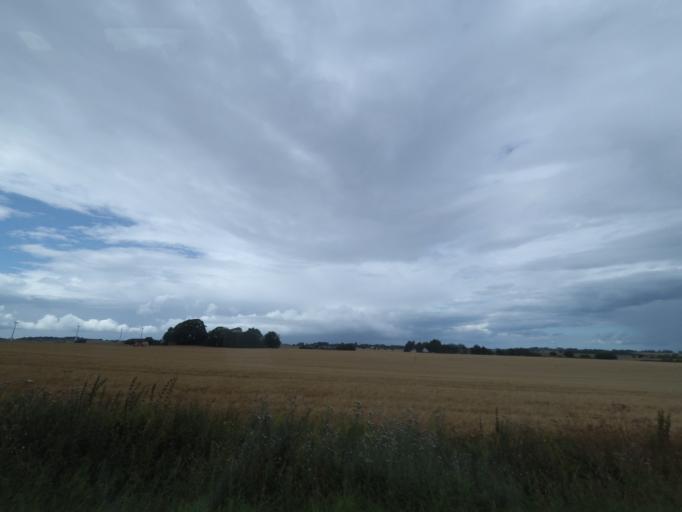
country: DK
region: South Denmark
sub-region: Nordfyns Kommune
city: Sonderso
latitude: 55.4972
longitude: 10.2495
